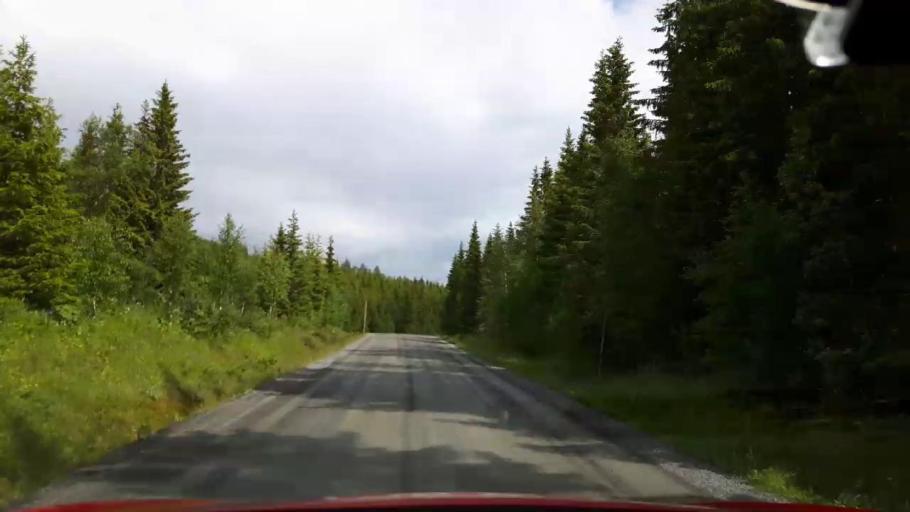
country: NO
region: Nord-Trondelag
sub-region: Lierne
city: Sandvika
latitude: 64.1447
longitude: 13.9056
